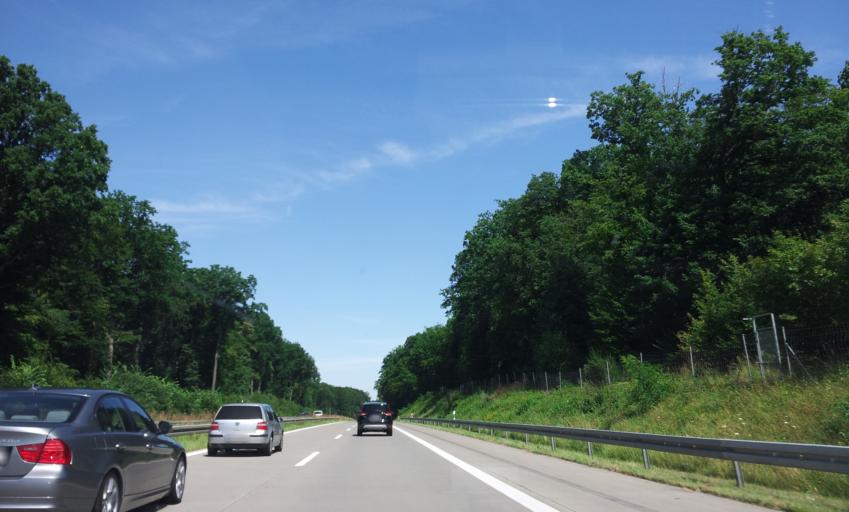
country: DE
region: Brandenburg
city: Althuttendorf
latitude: 52.9866
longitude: 13.8202
